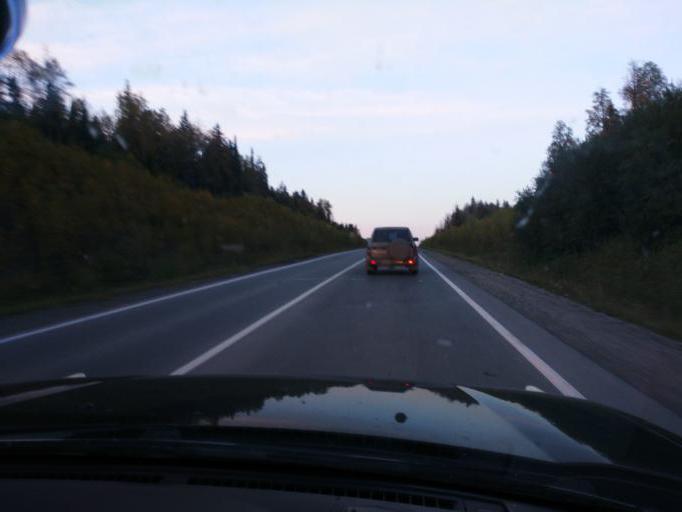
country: RU
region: Perm
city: Sylva
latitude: 58.2865
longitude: 56.7405
